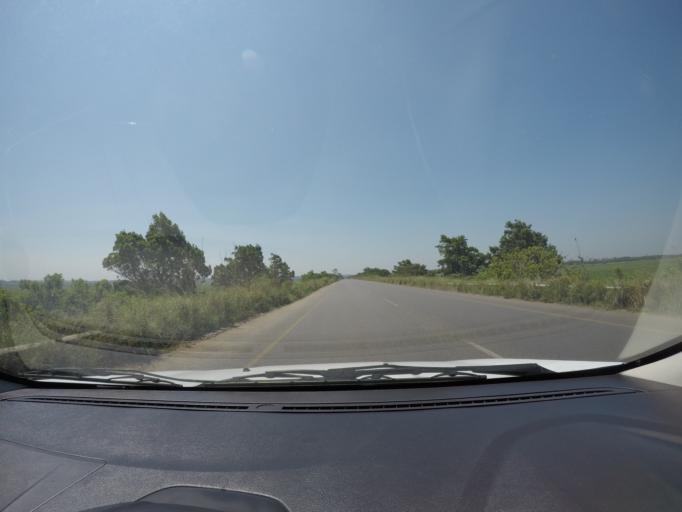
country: ZA
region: KwaZulu-Natal
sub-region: uThungulu District Municipality
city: Empangeni
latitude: -28.7934
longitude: 31.9580
